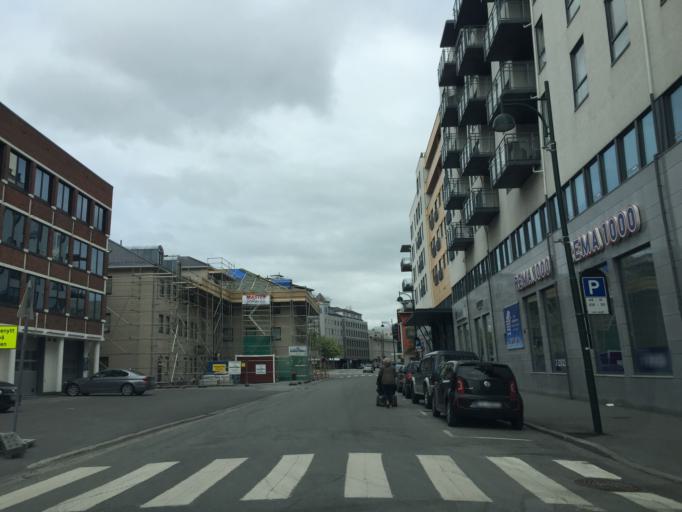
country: NO
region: Nordland
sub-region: Bodo
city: Bodo
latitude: 67.2836
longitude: 14.3753
